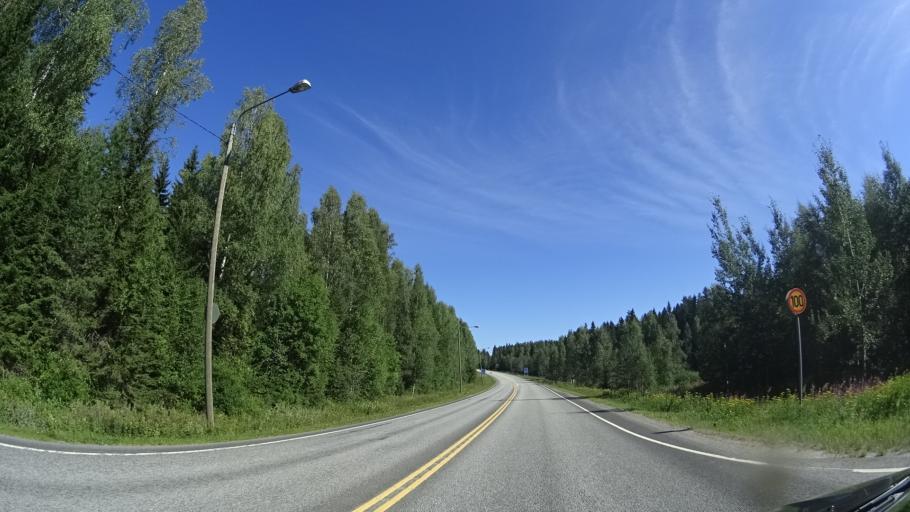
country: FI
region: Central Finland
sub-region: AEaenekoski
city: AEaenekoski
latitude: 62.8285
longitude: 25.8137
